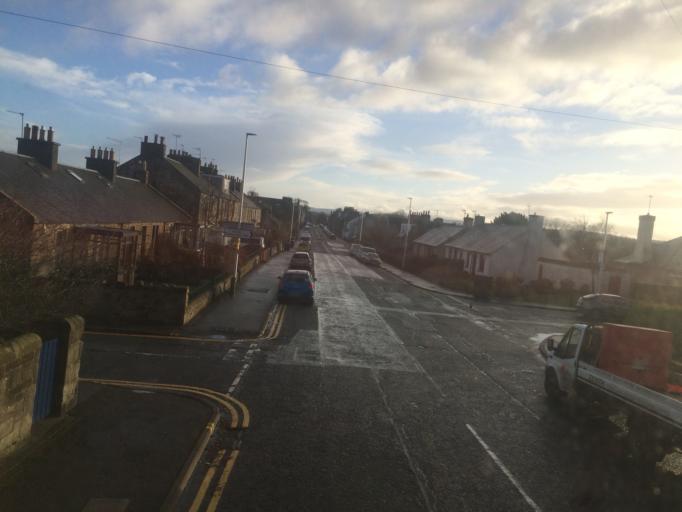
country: GB
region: Scotland
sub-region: Midlothian
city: Loanhead
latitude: 55.8595
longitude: -3.1679
